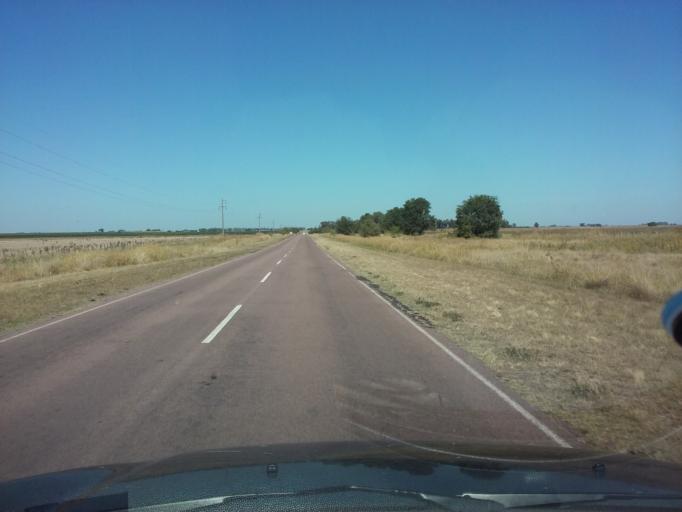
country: AR
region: La Pampa
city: Colonia Baron
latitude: -36.2556
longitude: -63.9428
